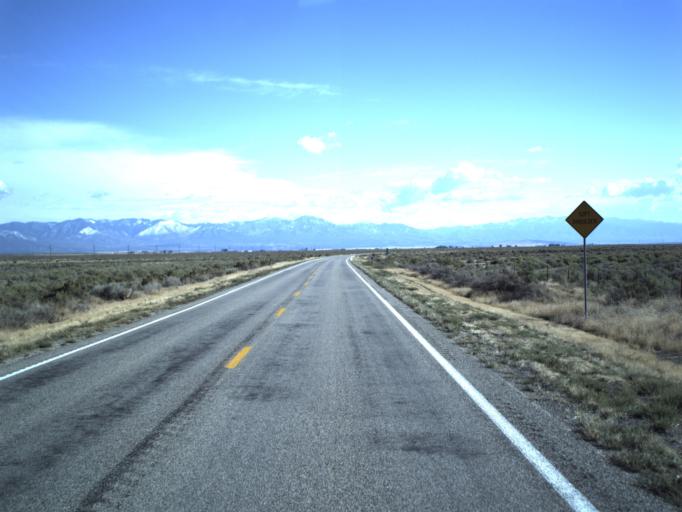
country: US
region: Utah
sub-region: Millard County
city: Delta
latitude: 39.2608
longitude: -112.4467
